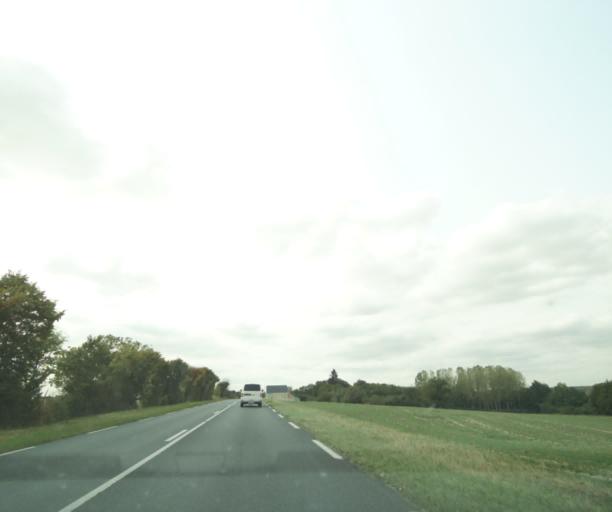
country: FR
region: Centre
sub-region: Departement de l'Indre
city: Chatillon-sur-Indre
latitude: 47.0004
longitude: 1.1485
